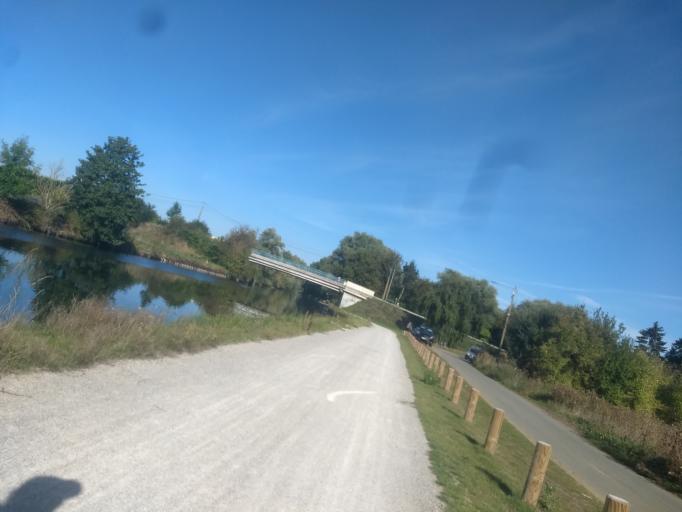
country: FR
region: Nord-Pas-de-Calais
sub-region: Departement du Pas-de-Calais
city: Roeux
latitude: 50.2921
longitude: 2.8988
